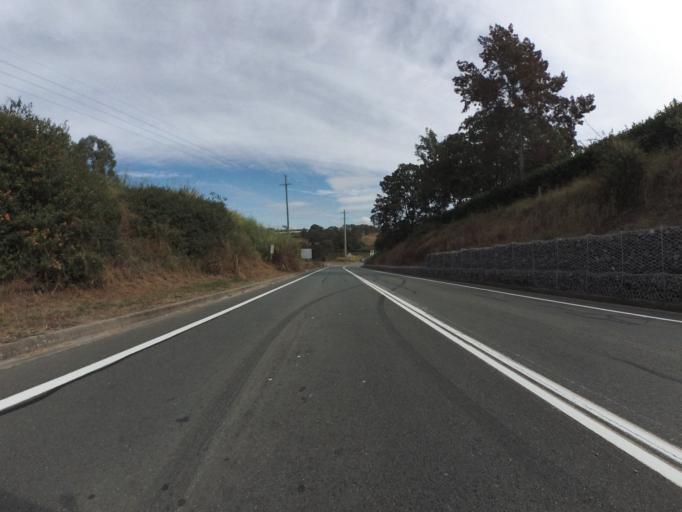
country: AU
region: Queensland
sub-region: Ipswich
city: Redbank
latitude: -27.5944
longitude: 152.8588
